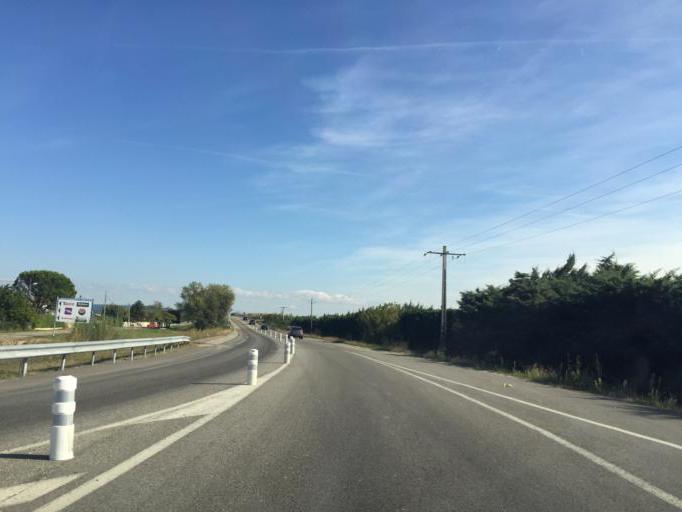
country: FR
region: Rhone-Alpes
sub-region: Departement de la Drome
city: Pierrelatte
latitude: 44.3601
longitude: 4.6961
